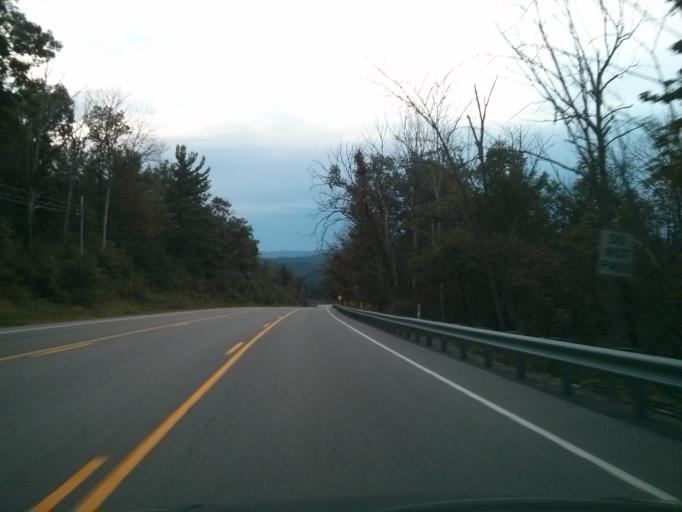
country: US
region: Pennsylvania
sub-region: Centre County
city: Stormstown
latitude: 40.8288
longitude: -78.0005
